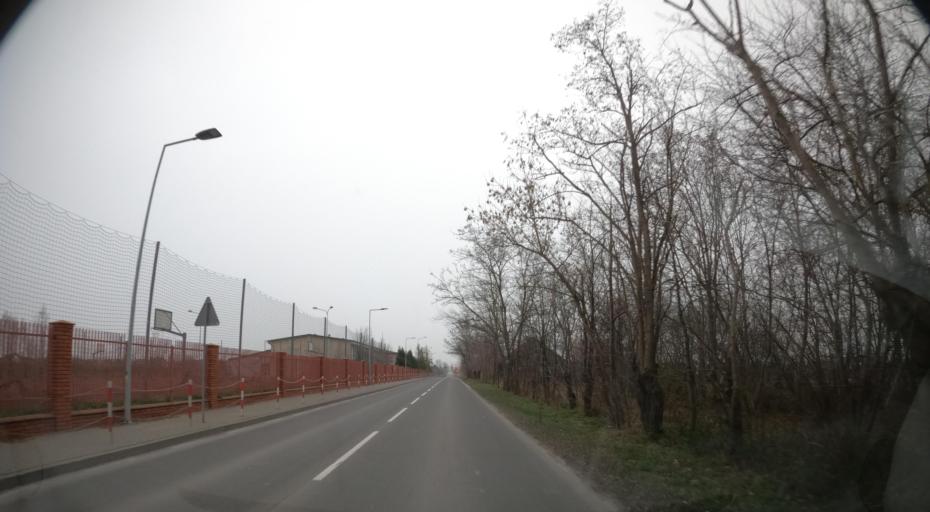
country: PL
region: Masovian Voivodeship
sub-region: Radom
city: Radom
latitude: 51.4400
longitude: 21.1888
